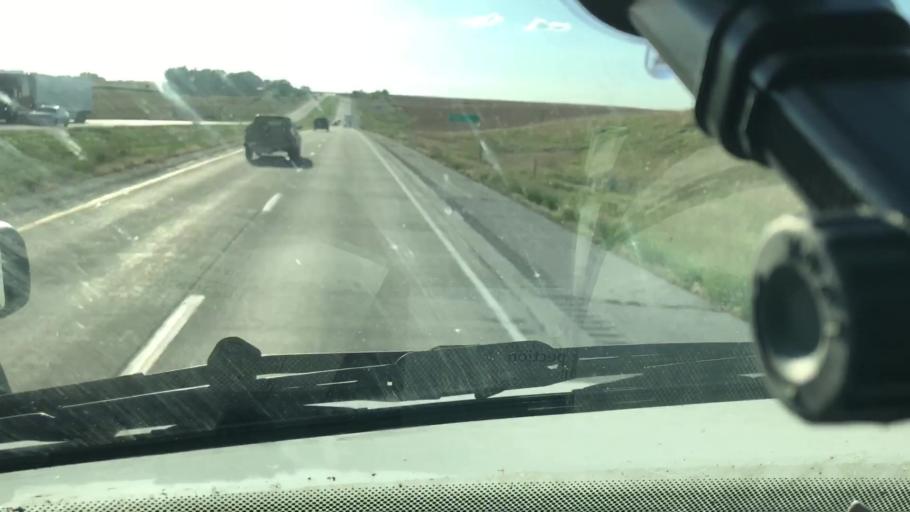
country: US
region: Iowa
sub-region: Pottawattamie County
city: Avoca
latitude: 41.4991
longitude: -95.4664
